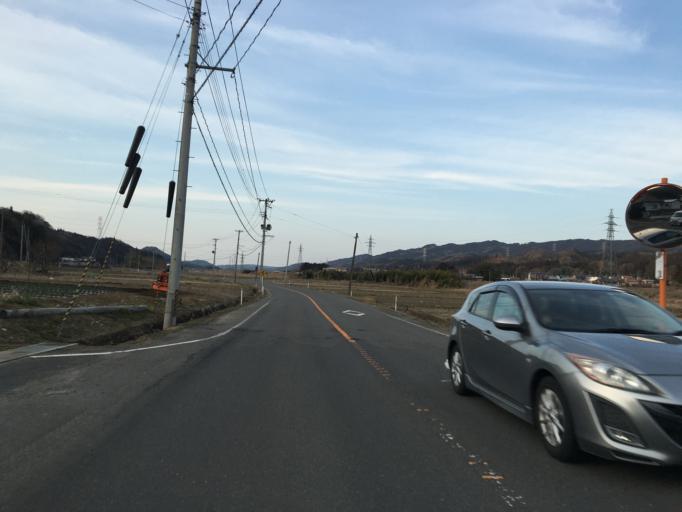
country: JP
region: Ibaraki
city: Daigo
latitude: 36.8776
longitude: 140.4152
